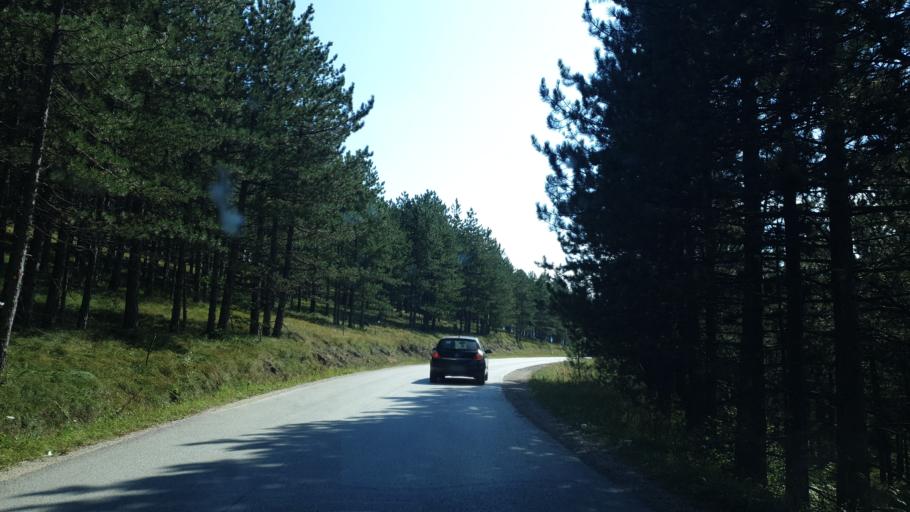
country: RS
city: Zlatibor
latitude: 43.7201
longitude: 19.7224
